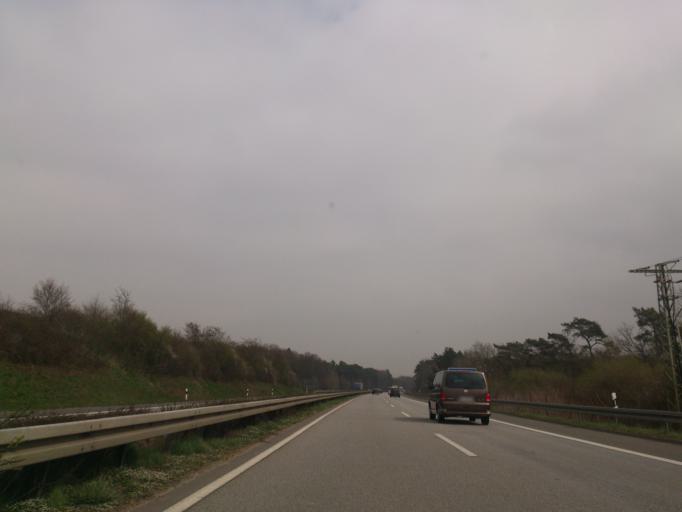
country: DE
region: North Rhine-Westphalia
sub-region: Regierungsbezirk Dusseldorf
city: Niederkruchten
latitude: 51.2089
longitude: 6.2386
